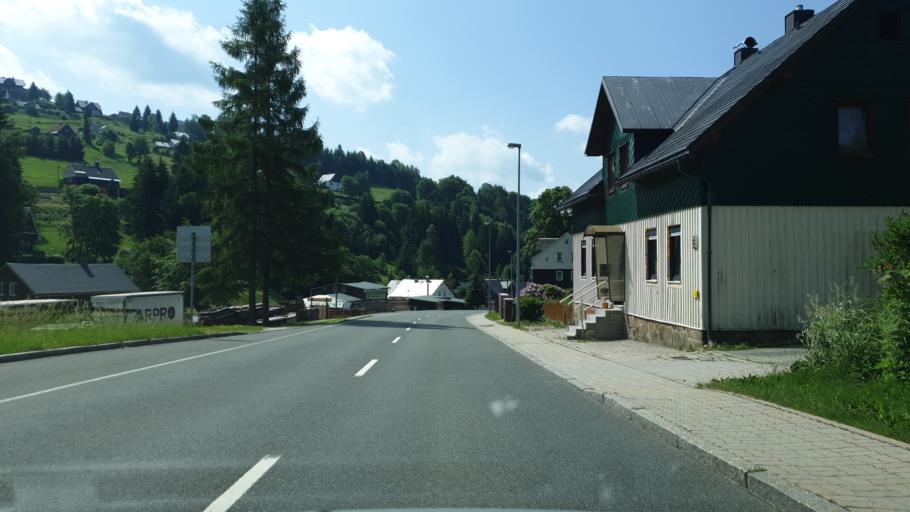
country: DE
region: Saxony
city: Klingenthal
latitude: 50.3923
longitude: 12.4949
